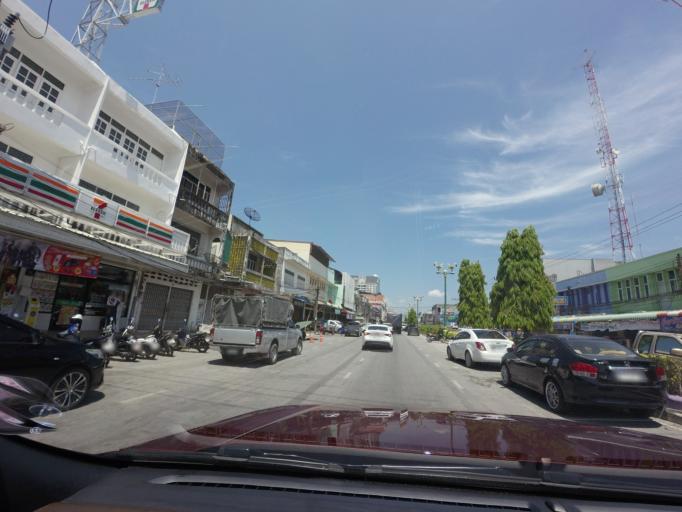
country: TH
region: Yala
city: Yala
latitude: 6.5592
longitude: 101.2893
